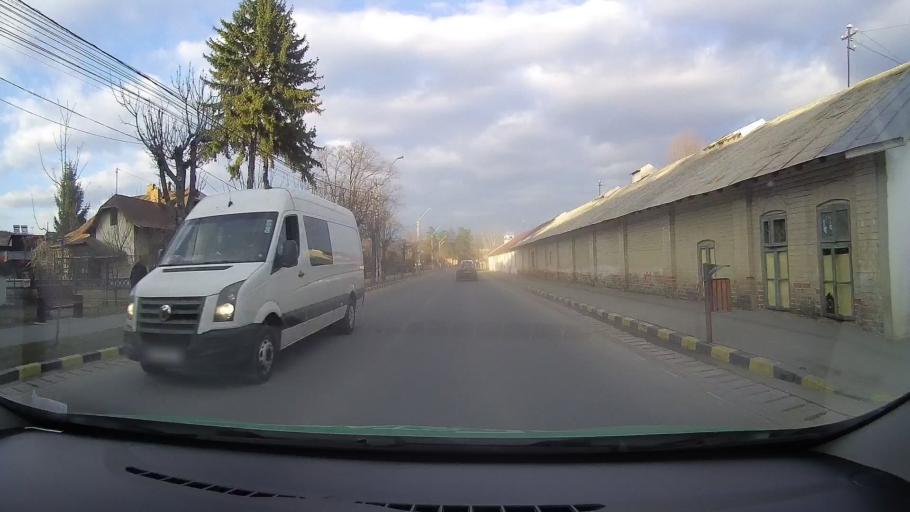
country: RO
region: Dambovita
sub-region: Municipiul Moreni
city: Moreni
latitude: 44.9803
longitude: 25.6381
